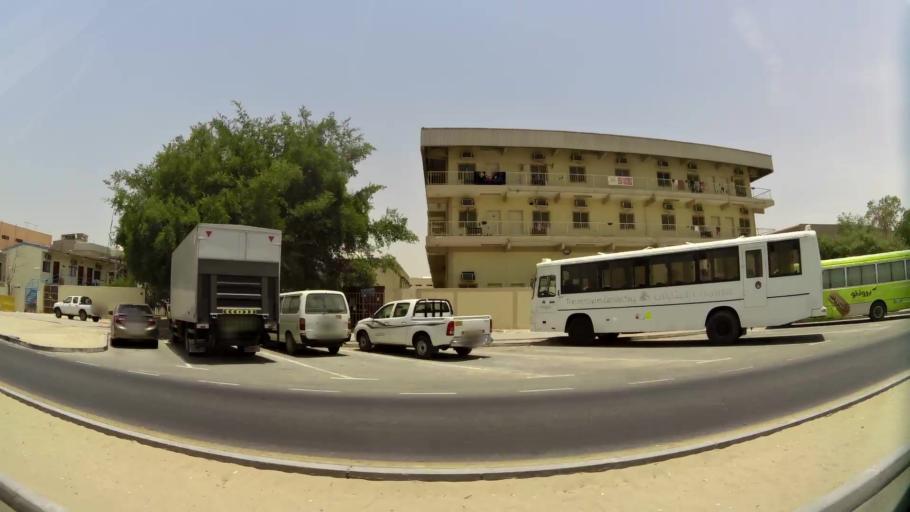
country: AE
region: Ash Shariqah
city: Sharjah
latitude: 25.2708
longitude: 55.4329
